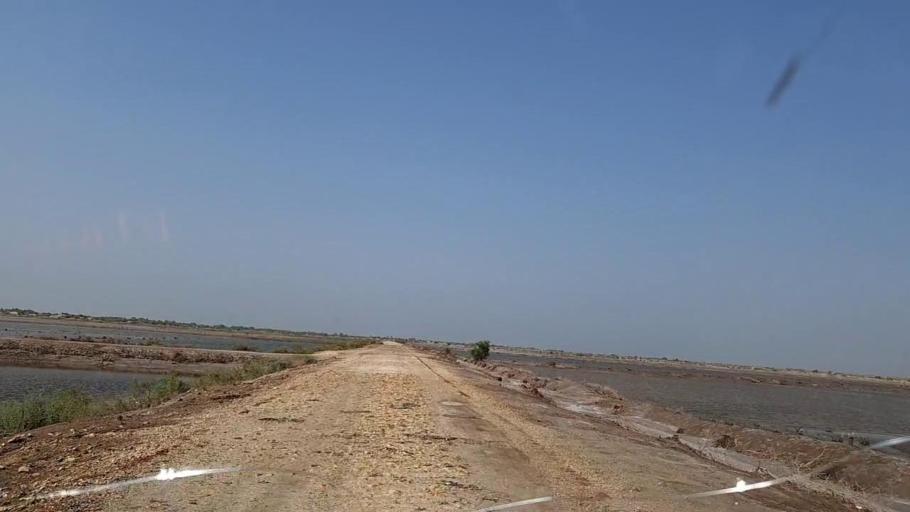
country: PK
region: Sindh
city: Khanpur
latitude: 27.6871
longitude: 69.3808
